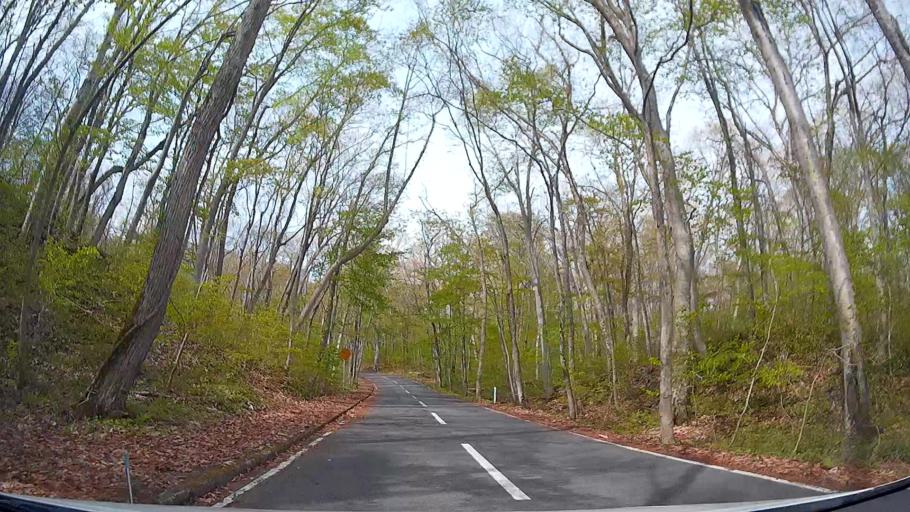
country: JP
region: Akita
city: Hanawa
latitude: 40.4337
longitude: 140.9156
